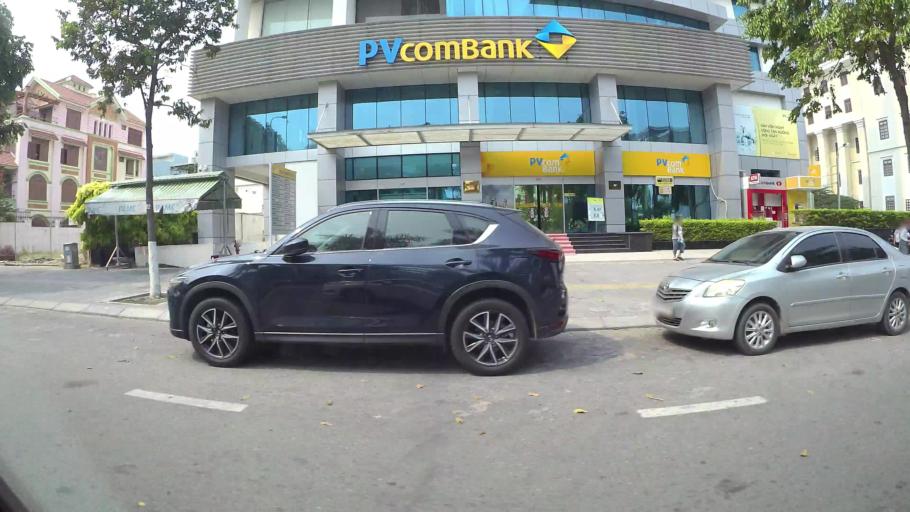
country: VN
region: Da Nang
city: Son Tra
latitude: 16.0408
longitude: 108.2206
